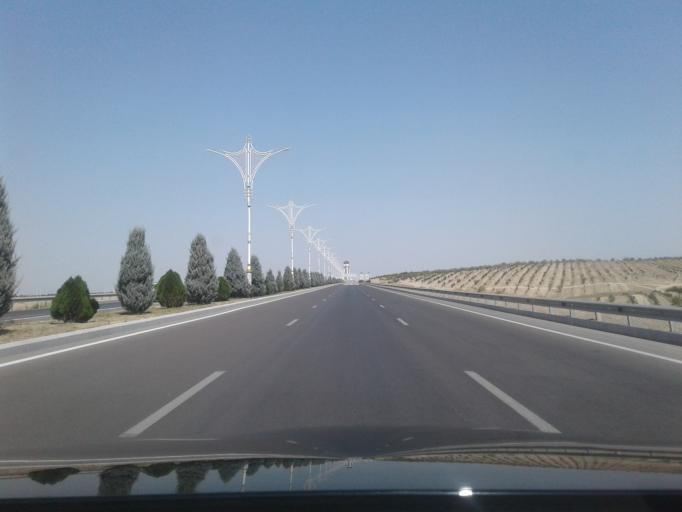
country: TM
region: Ahal
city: Ashgabat
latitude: 37.8783
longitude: 58.4109
